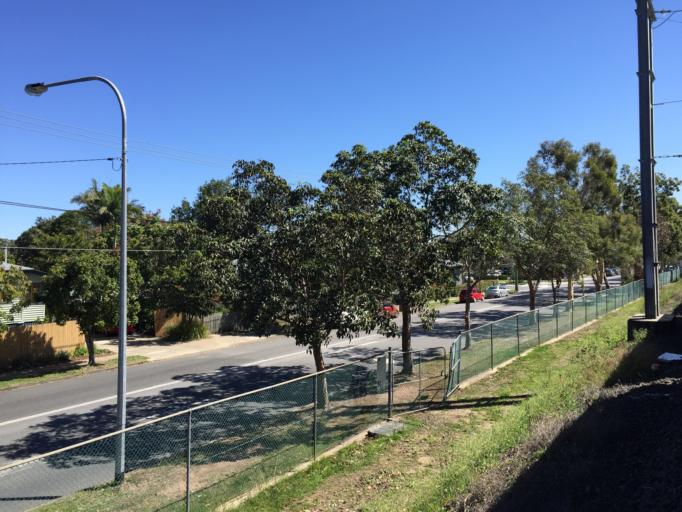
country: AU
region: Queensland
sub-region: Brisbane
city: Rocklea
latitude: -27.5240
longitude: 152.9774
